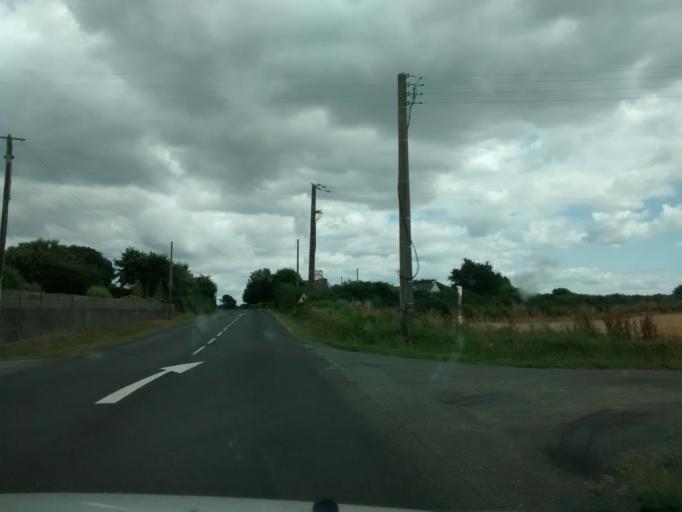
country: FR
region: Brittany
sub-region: Departement du Finistere
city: Plouneventer
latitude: 48.5593
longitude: -4.2322
